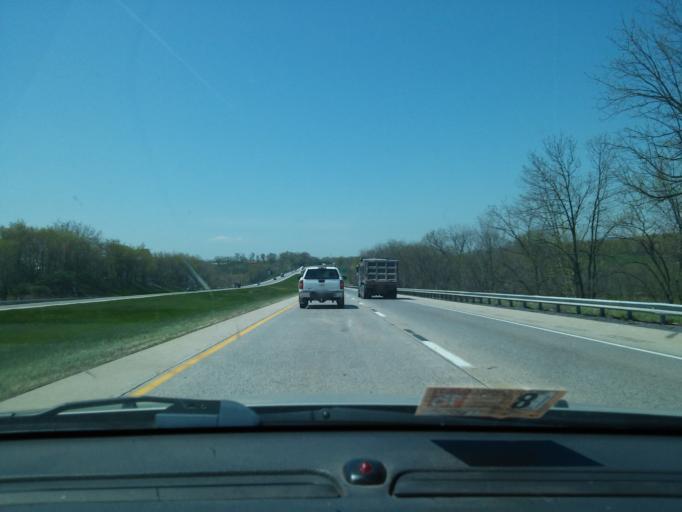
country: US
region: Pennsylvania
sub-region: Lebanon County
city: Jonestown
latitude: 40.4190
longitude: -76.5496
